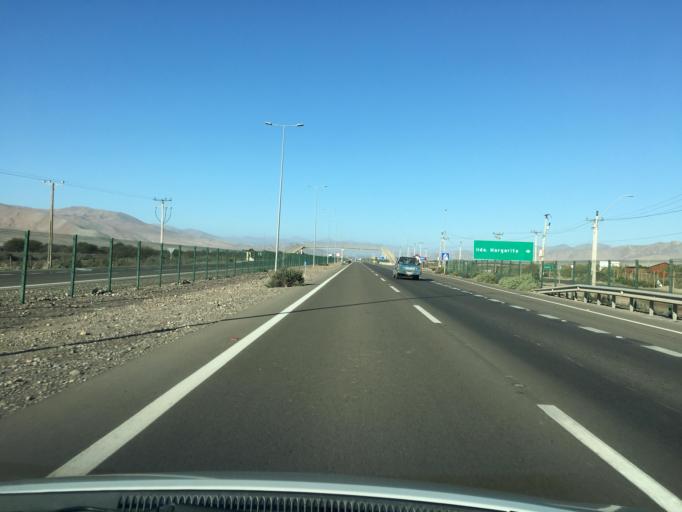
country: CL
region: Atacama
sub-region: Provincia de Copiapo
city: Copiapo
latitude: -27.3397
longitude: -70.6017
